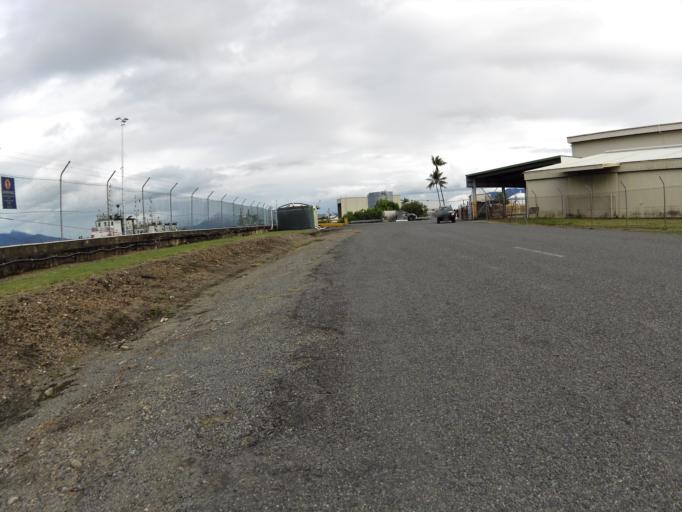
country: AU
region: Queensland
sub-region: Cairns
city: Cairns
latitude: -16.9315
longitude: 145.7792
